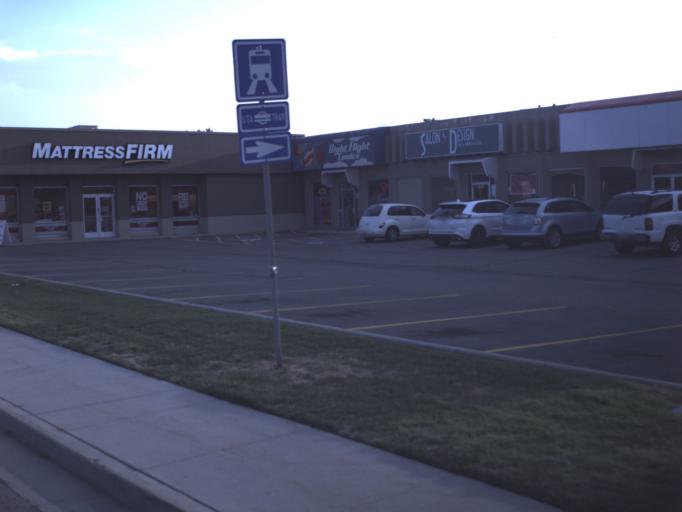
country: US
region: Utah
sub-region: Salt Lake County
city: Midvale
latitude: 40.6359
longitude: -111.8894
